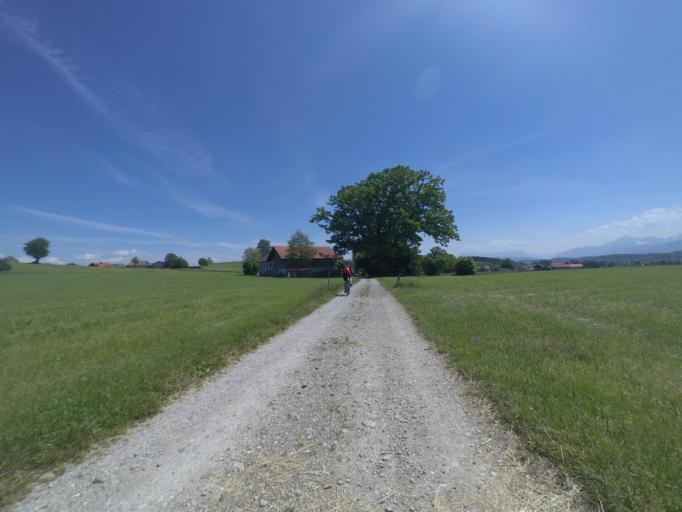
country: DE
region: Bavaria
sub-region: Upper Bavaria
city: Petting
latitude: 47.9373
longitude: 12.8013
